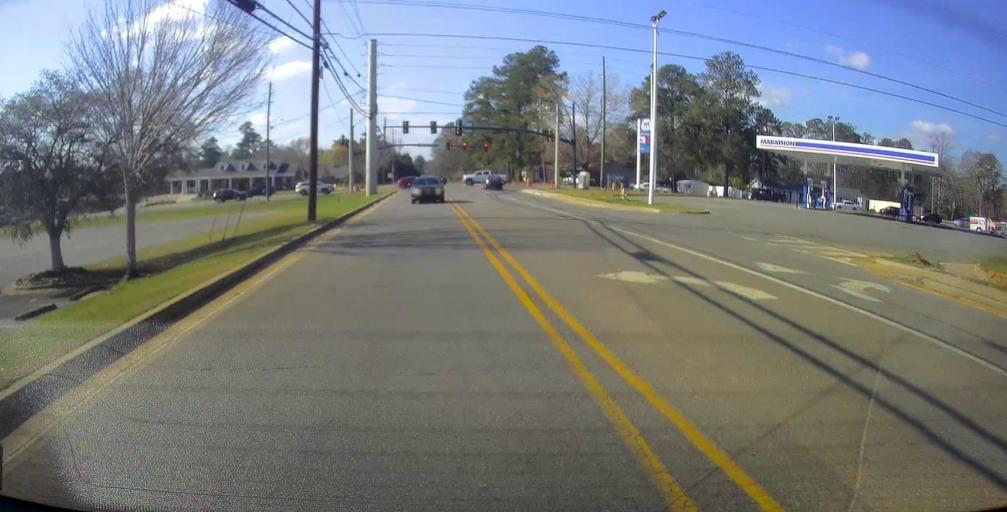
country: US
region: Georgia
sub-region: Laurens County
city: Dublin
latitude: 32.5487
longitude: -82.9255
